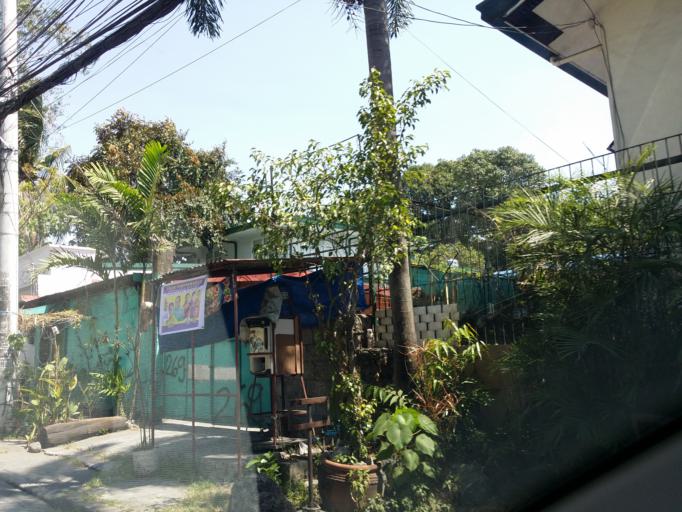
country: PH
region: Metro Manila
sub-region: Mandaluyong
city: Mandaluyong City
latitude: 14.5861
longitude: 121.0308
